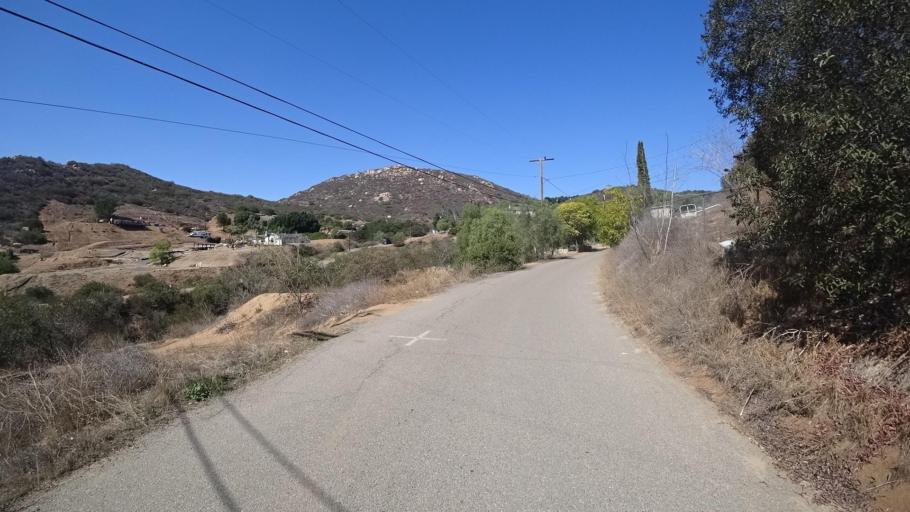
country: US
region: California
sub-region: San Diego County
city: Harbison Canyon
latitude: 32.8160
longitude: -116.8370
